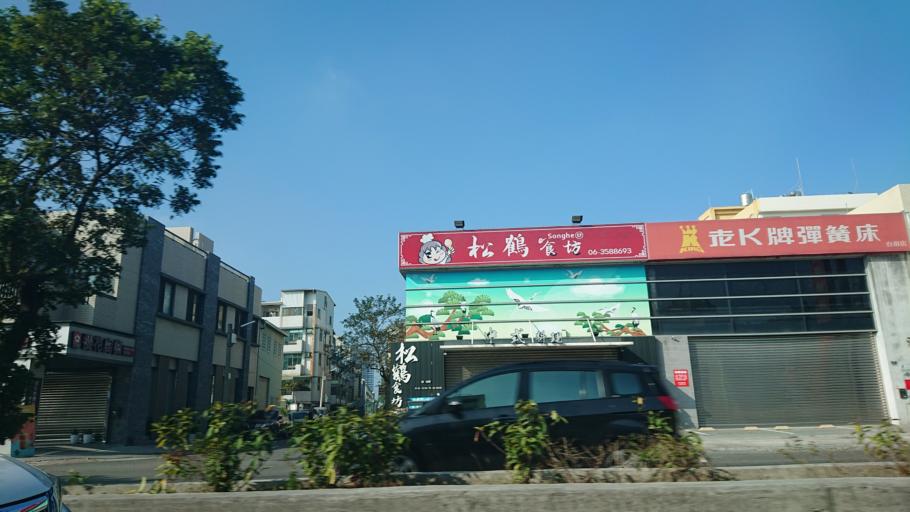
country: TW
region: Taiwan
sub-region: Tainan
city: Tainan
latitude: 23.0091
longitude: 120.1856
